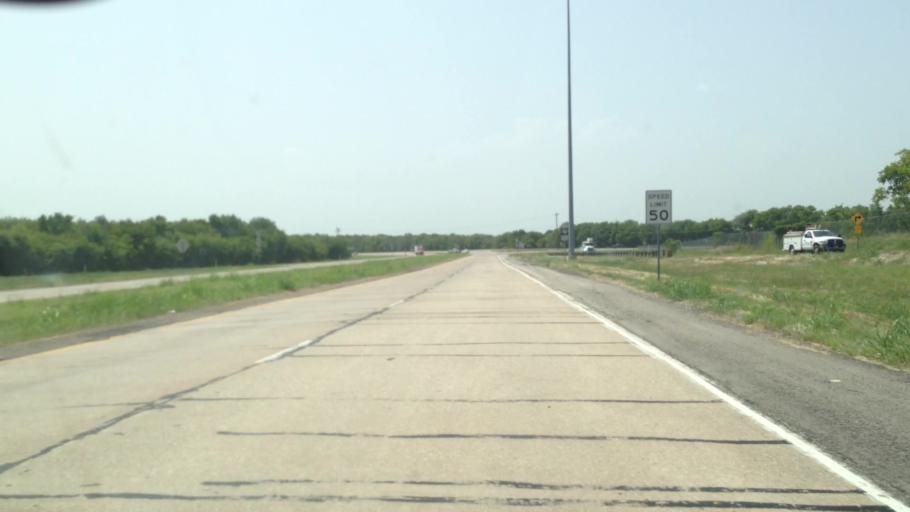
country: US
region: Texas
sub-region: Hunt County
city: Greenville
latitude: 33.1369
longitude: -96.0746
